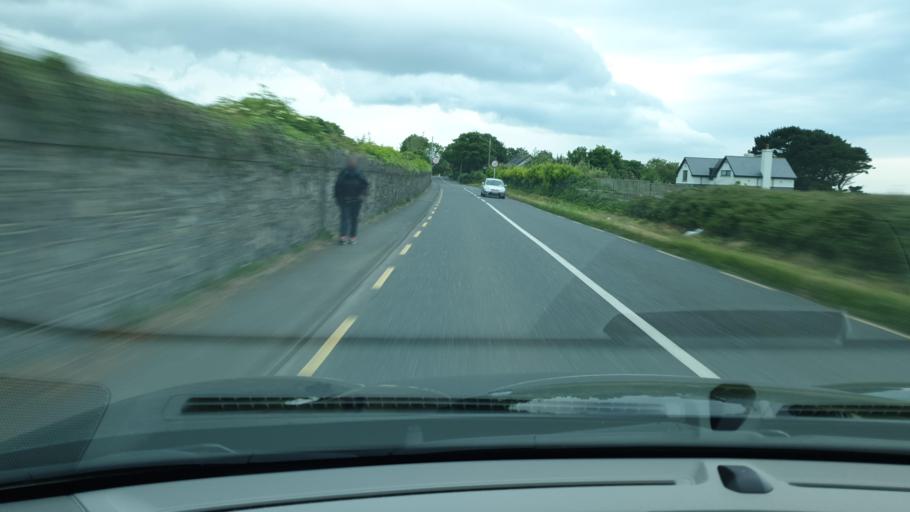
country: IE
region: Leinster
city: Balbriggan
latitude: 53.6009
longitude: -6.1654
